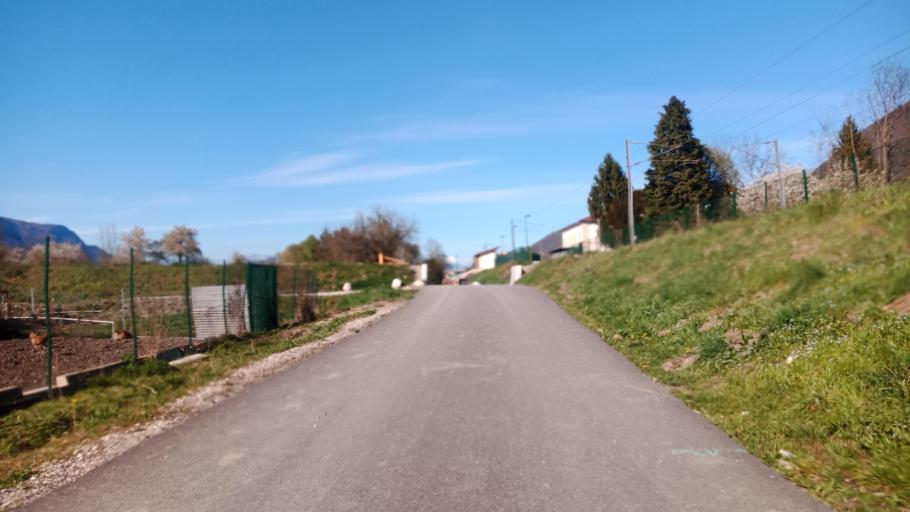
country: FR
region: Rhone-Alpes
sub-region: Departement de l'Isere
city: Goncelin
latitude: 45.3410
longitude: 5.9731
